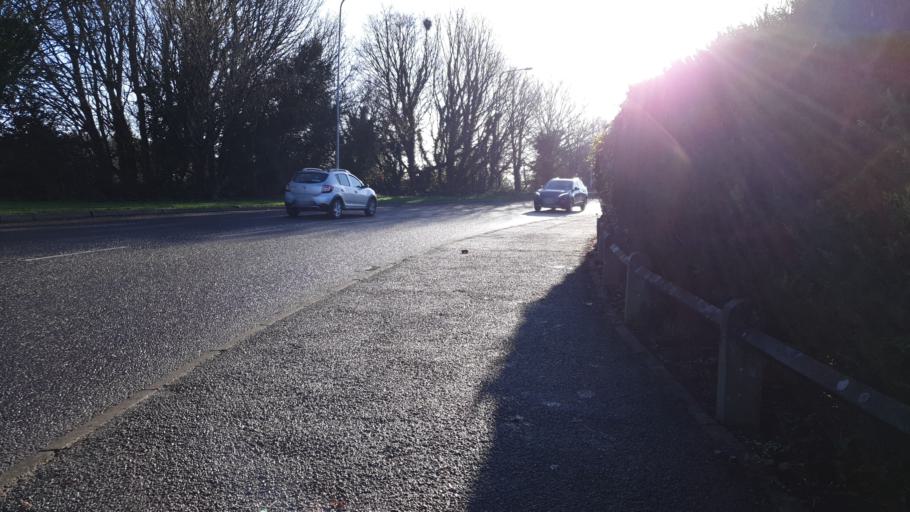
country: IE
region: Munster
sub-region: County Cork
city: Cork
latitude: 51.8915
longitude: -8.4337
